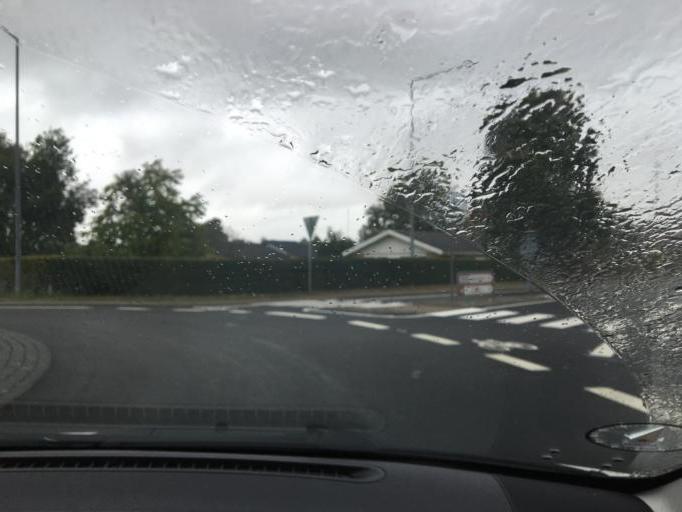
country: DK
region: South Denmark
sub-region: Middelfart Kommune
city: Middelfart
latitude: 55.4914
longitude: 9.7619
